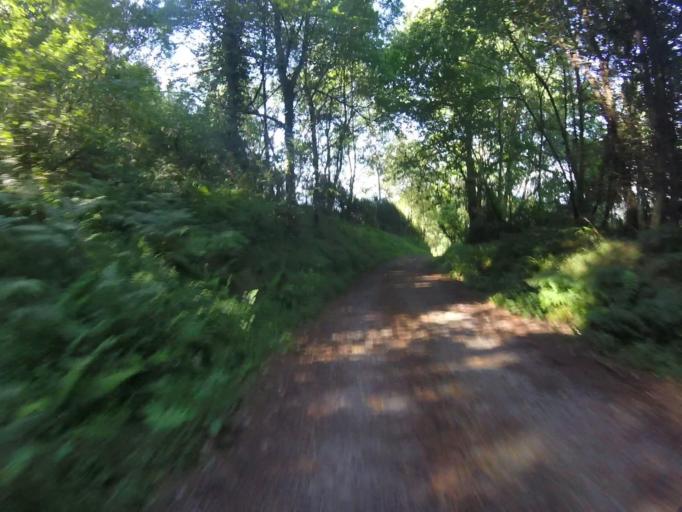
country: ES
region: Basque Country
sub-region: Provincia de Guipuzcoa
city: Irun
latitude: 43.3098
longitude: -1.7815
